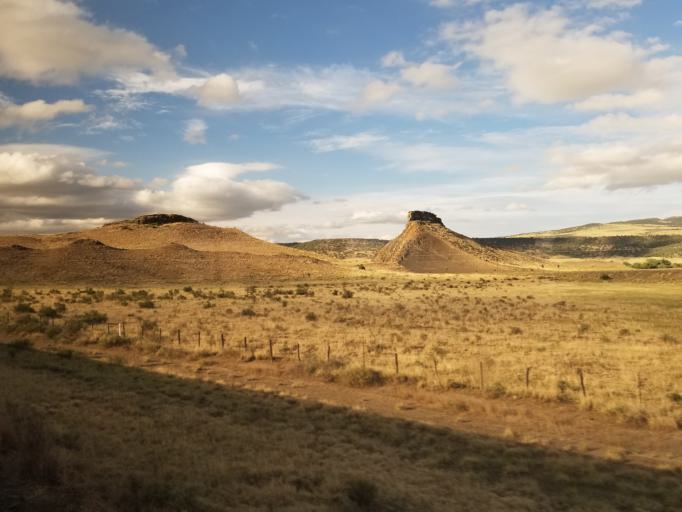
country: US
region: New Mexico
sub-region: Colfax County
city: Raton
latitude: 36.6625
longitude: -104.4980
